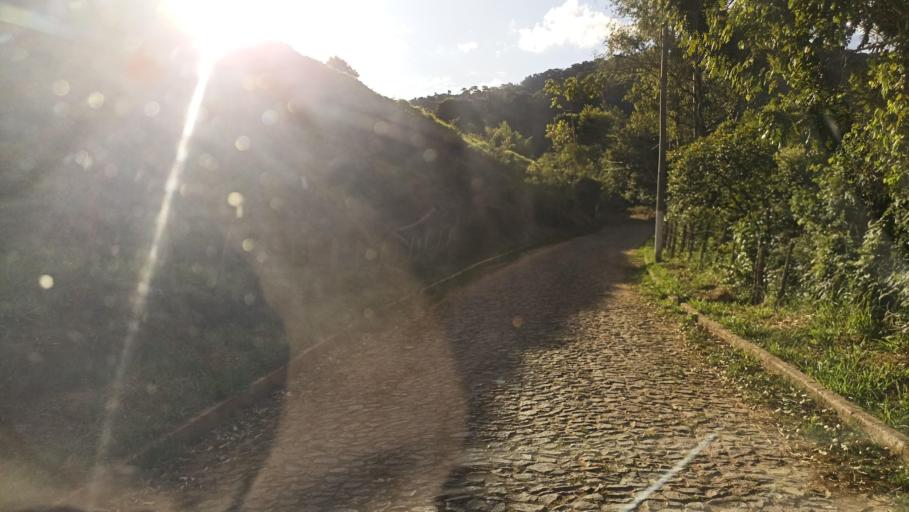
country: BR
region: Minas Gerais
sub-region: Ouro Preto
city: Ouro Preto
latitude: -20.3128
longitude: -43.5859
